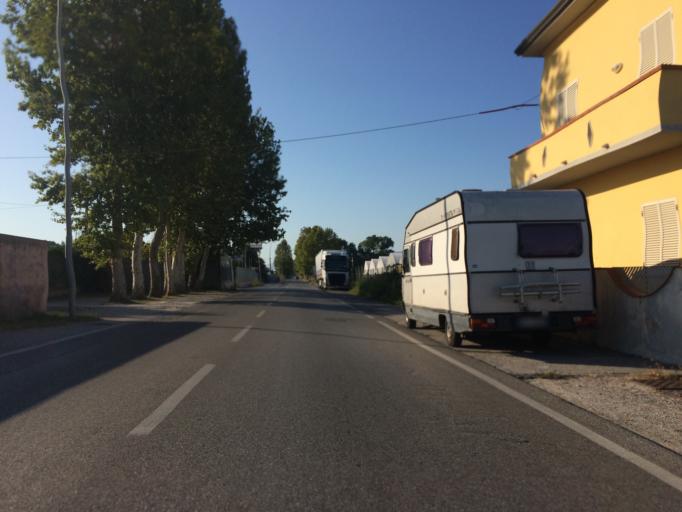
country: IT
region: Tuscany
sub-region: Provincia di Lucca
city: Torre del Lago Puccini
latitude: 43.8375
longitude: 10.2857
